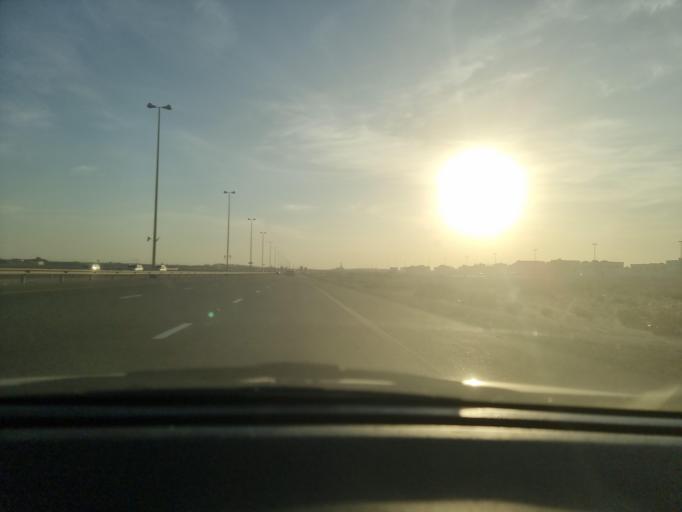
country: AE
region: Abu Dhabi
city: Abu Dhabi
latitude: 24.3487
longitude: 54.7085
